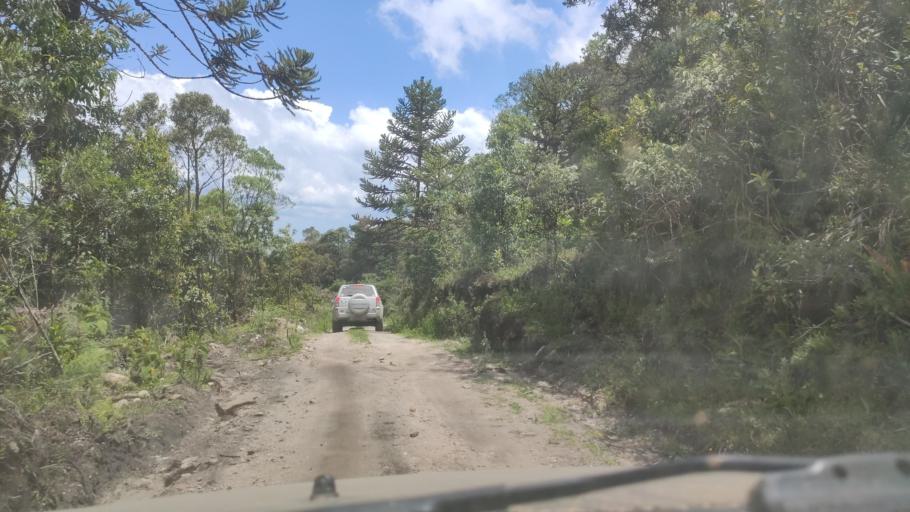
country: BR
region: Minas Gerais
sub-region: Cambui
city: Cambui
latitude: -22.6916
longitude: -45.9589
